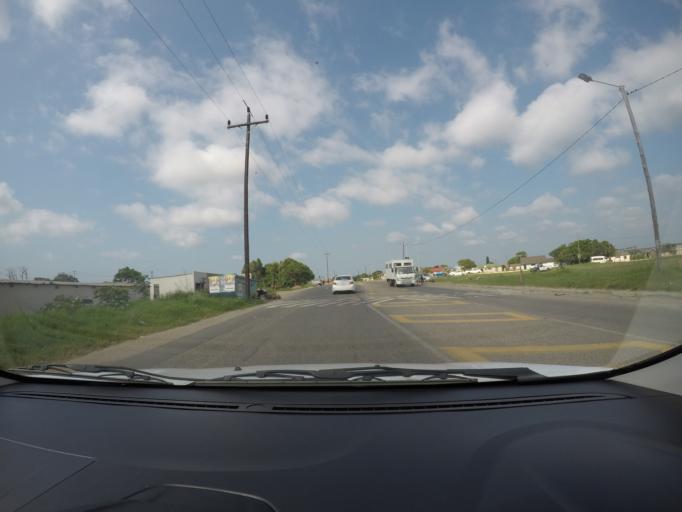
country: ZA
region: KwaZulu-Natal
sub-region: uThungulu District Municipality
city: eSikhawini
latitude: -28.8830
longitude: 31.9041
